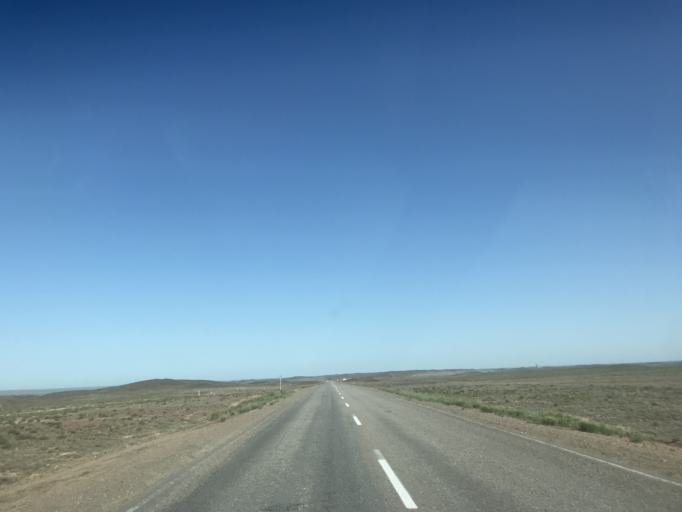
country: KZ
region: Zhambyl
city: Mynaral
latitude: 45.4662
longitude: 73.5674
